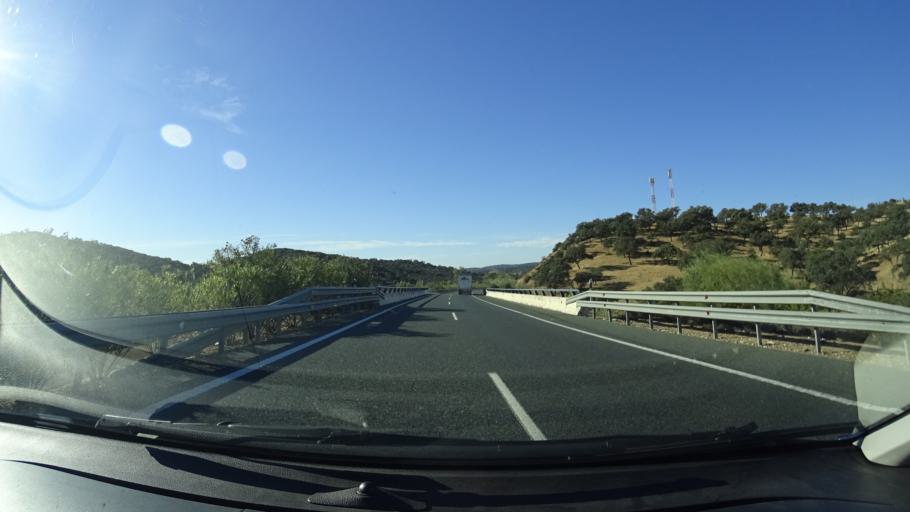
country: ES
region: Andalusia
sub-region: Provincia de Sevilla
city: El Ronquillo
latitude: 37.7603
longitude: -6.1662
